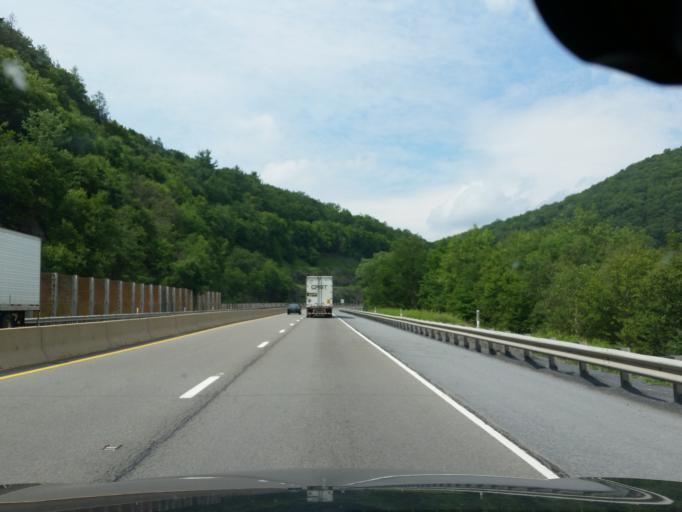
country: US
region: Pennsylvania
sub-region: Mifflin County
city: Milroy
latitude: 40.7286
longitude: -77.6218
